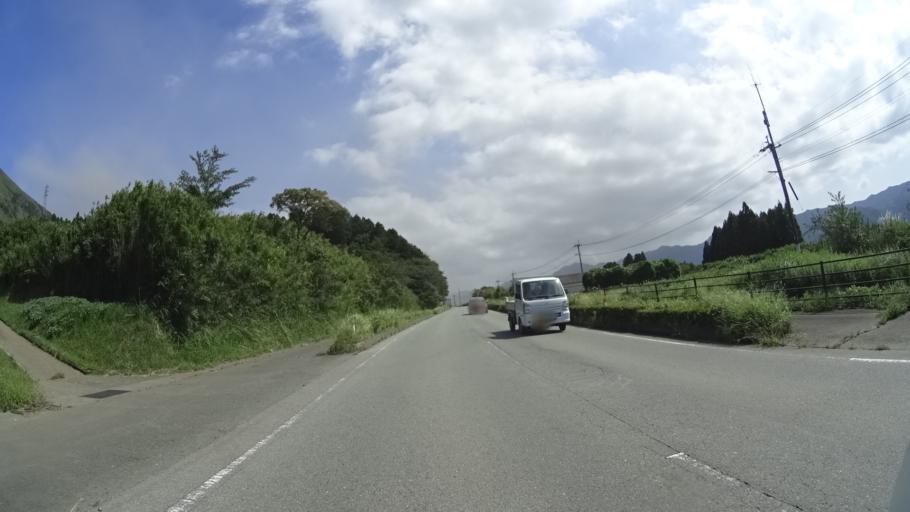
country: JP
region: Kumamoto
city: Aso
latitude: 32.8514
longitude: 131.0235
